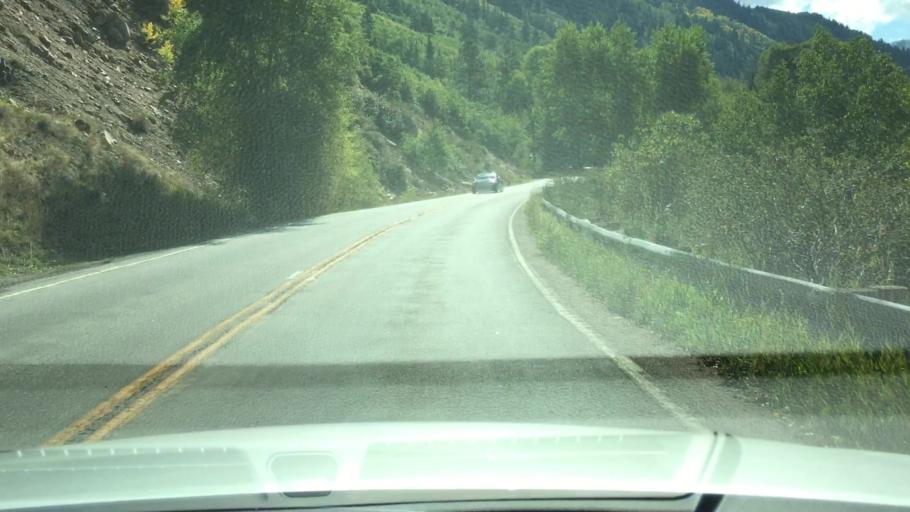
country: US
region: Colorado
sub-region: Pitkin County
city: Aspen
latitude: 39.1774
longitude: -106.7968
